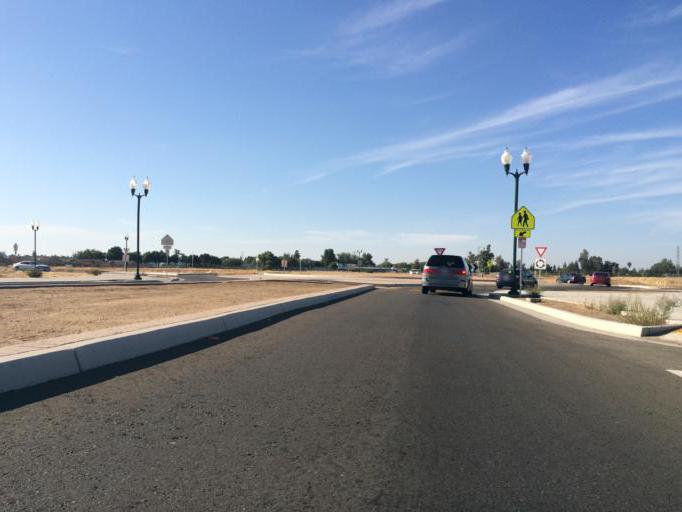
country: US
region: California
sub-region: Fresno County
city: Sunnyside
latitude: 36.7385
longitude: -119.6820
